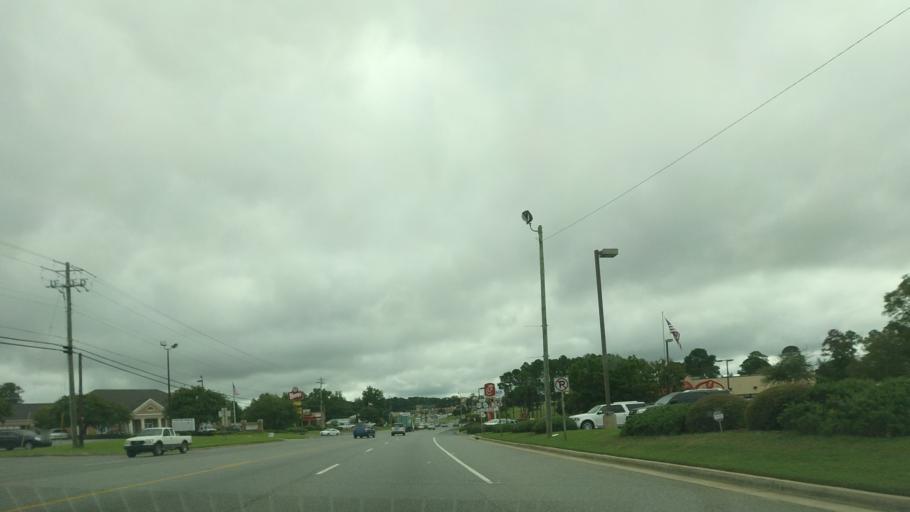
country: US
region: Georgia
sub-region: Laurens County
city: Dublin
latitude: 32.5412
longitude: -82.9490
